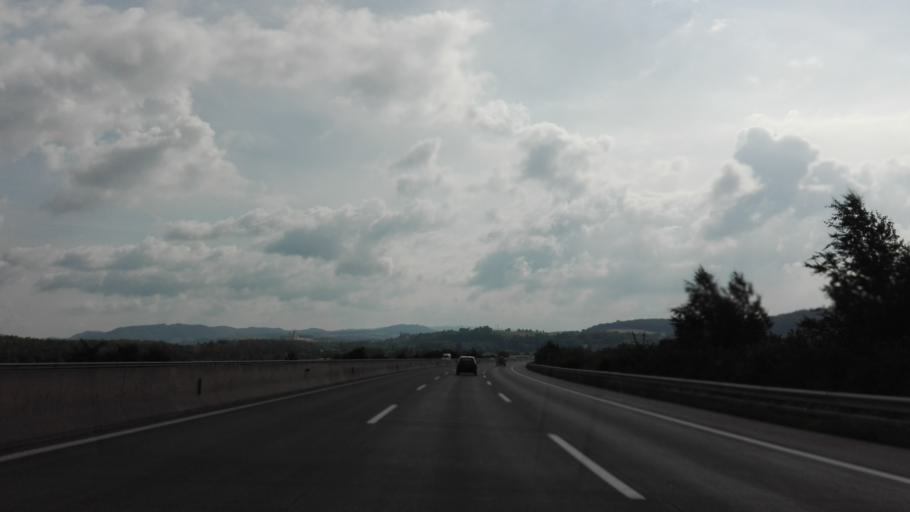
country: AT
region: Lower Austria
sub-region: Politischer Bezirk Melk
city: Leiben
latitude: 48.2153
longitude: 15.2898
